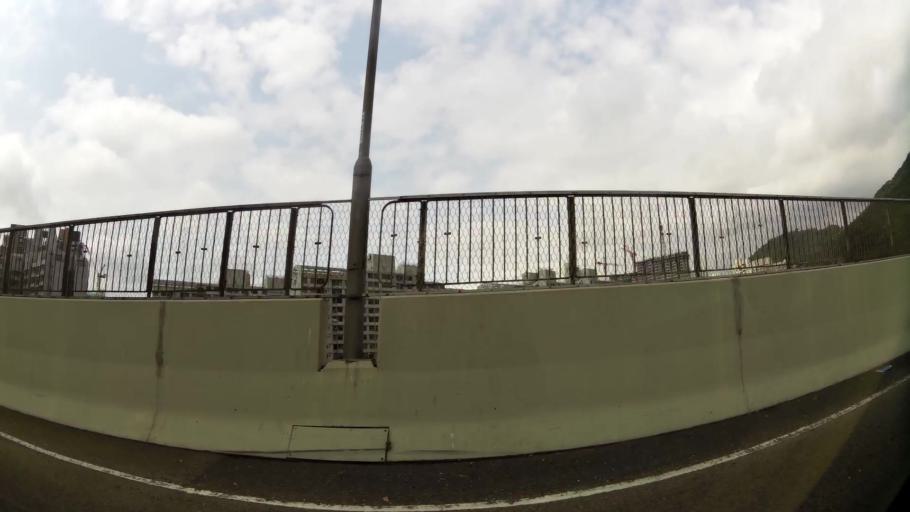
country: HK
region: Sham Shui Po
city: Sham Shui Po
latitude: 22.3395
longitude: 114.1618
